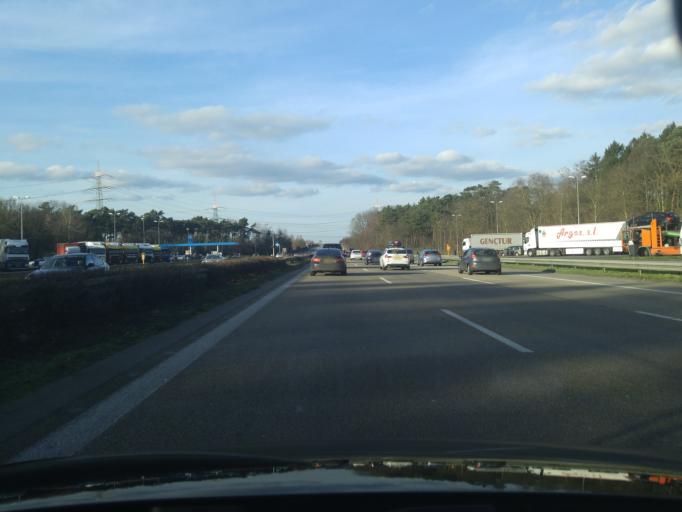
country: DE
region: North Rhine-Westphalia
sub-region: Regierungsbezirk Dusseldorf
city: Hilden
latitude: 51.1572
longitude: 6.9633
